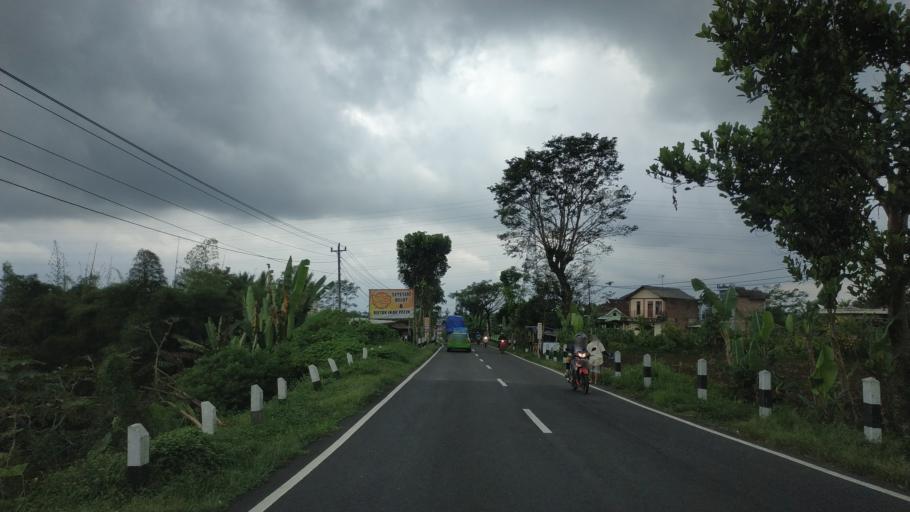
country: ID
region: Central Java
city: Magelang
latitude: -7.2875
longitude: 110.1246
